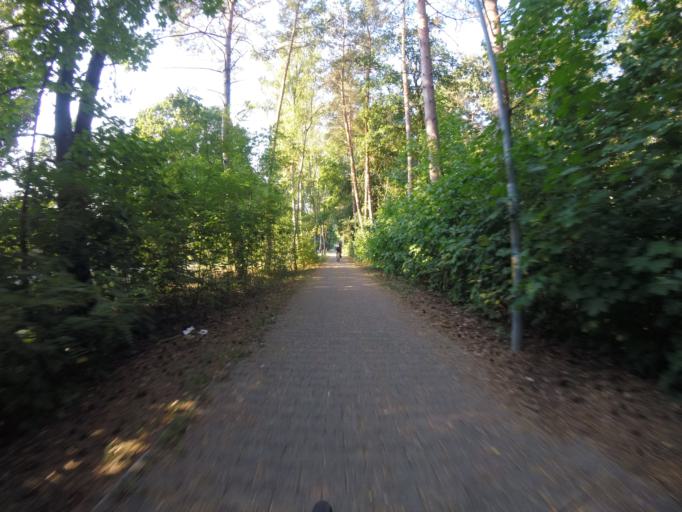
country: DE
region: Brandenburg
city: Grunheide
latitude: 52.4115
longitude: 13.8255
